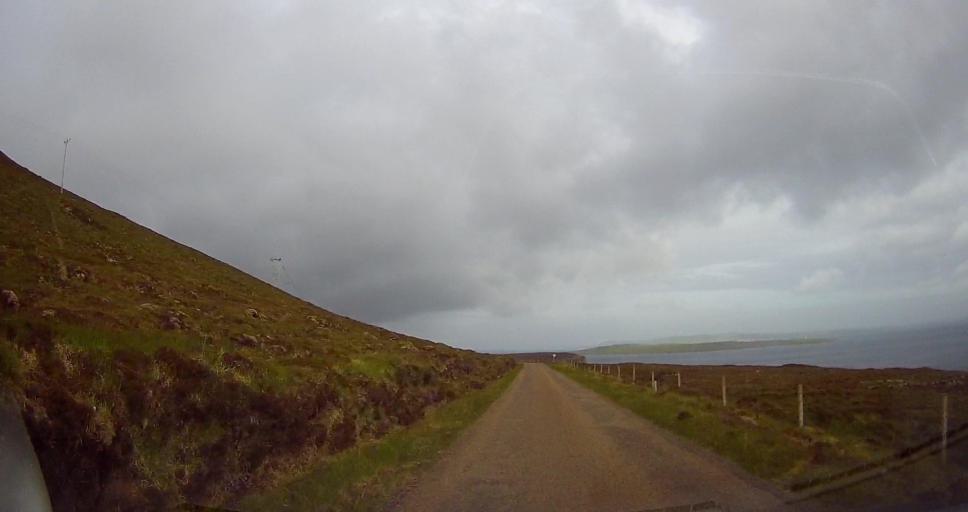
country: GB
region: Scotland
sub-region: Orkney Islands
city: Stromness
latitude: 58.8883
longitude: -3.2540
